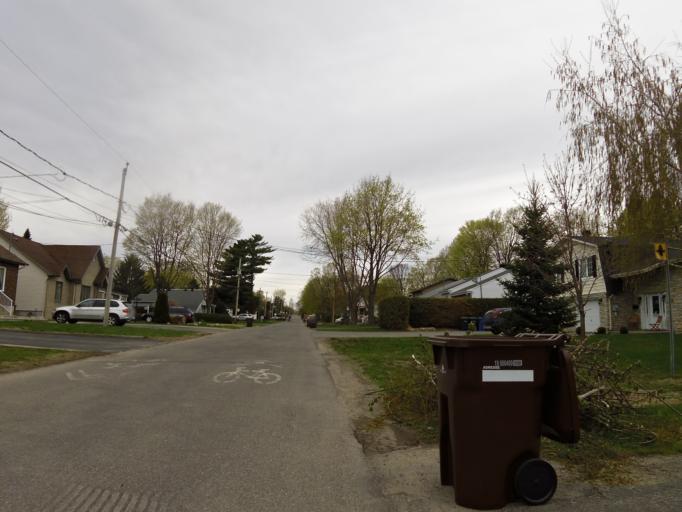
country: CA
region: Quebec
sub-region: Laurentides
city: Deux-Montagnes
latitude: 45.5379
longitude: -73.8998
